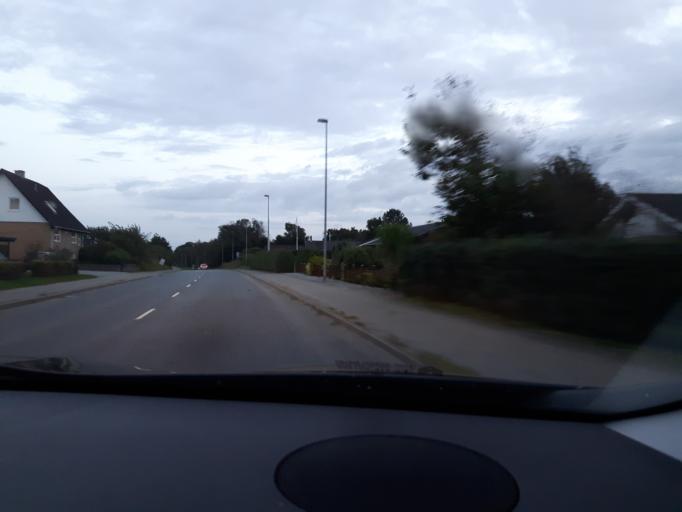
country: DK
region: North Denmark
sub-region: Hjorring Kommune
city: Hirtshals
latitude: 57.5315
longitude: 9.9467
